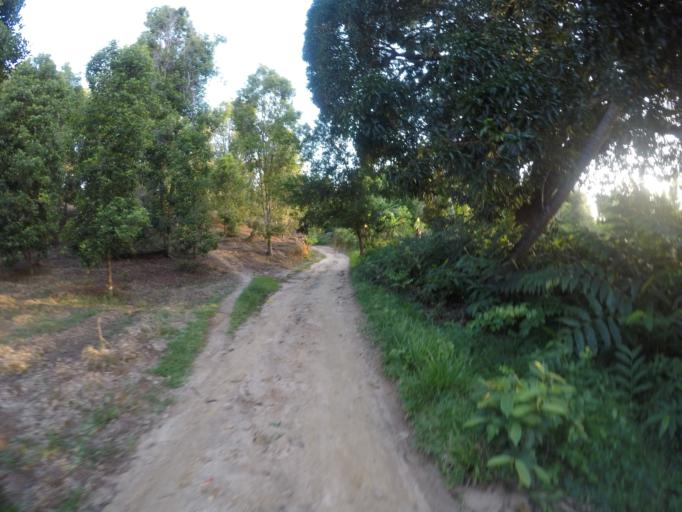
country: TZ
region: Pemba South
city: Mtambile
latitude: -5.3793
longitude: 39.7078
